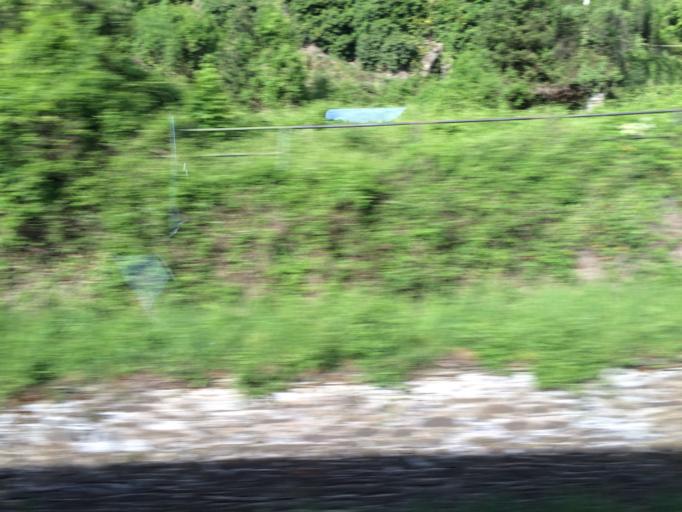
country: DE
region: Rheinland-Pfalz
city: Dorscheid
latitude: 50.0944
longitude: 7.7538
